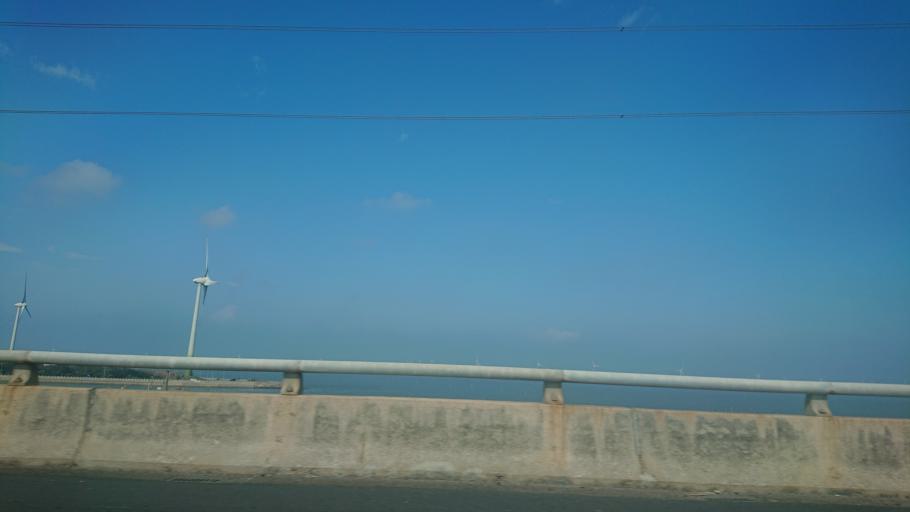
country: TW
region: Taiwan
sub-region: Changhua
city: Chang-hua
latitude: 24.0840
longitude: 120.4228
